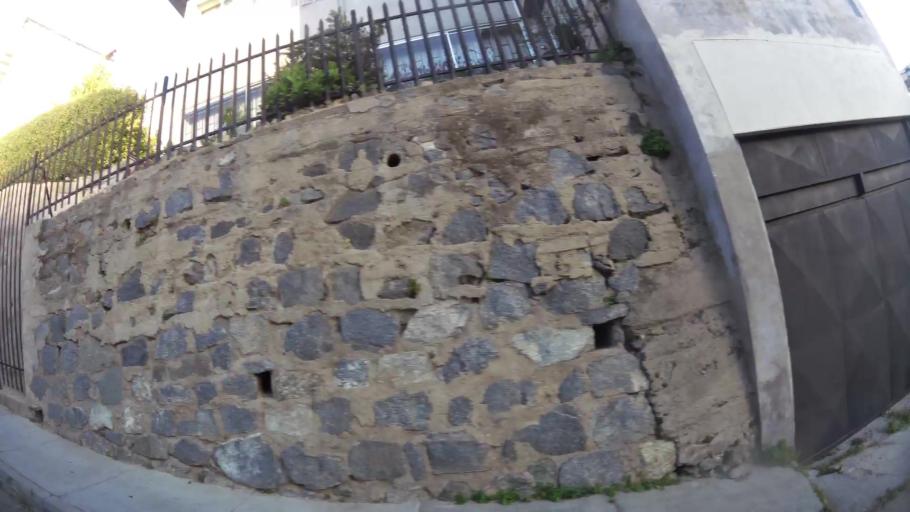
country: CL
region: Valparaiso
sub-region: Provincia de Valparaiso
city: Valparaiso
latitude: -33.0542
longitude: -71.6053
